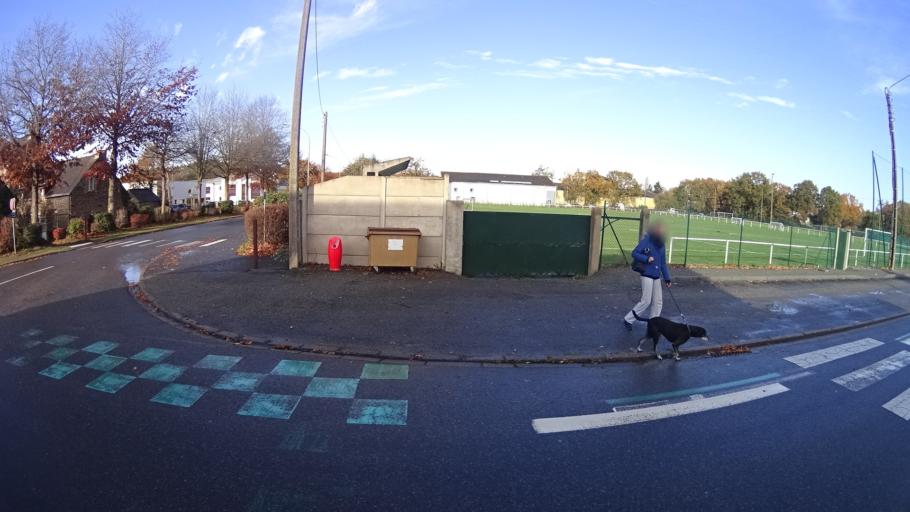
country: FR
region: Brittany
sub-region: Departement d'Ille-et-Vilaine
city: Redon
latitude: 47.6635
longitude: -2.0730
